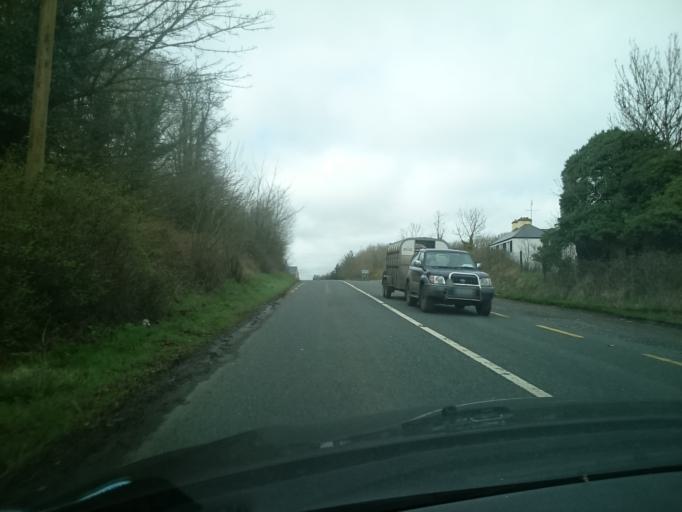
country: IE
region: Connaught
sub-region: Maigh Eo
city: Kiltamagh
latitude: 53.8122
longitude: -9.1480
